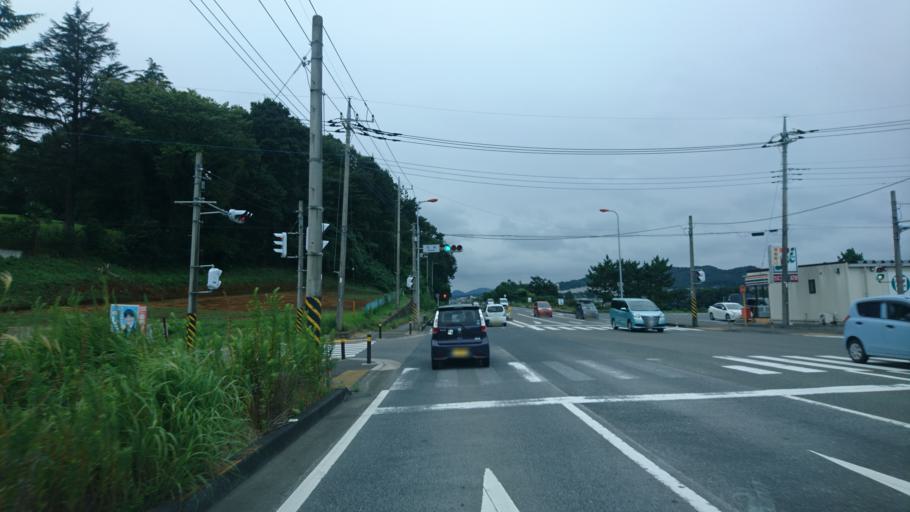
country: JP
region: Kanagawa
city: Atsugi
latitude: 35.4764
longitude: 139.3357
